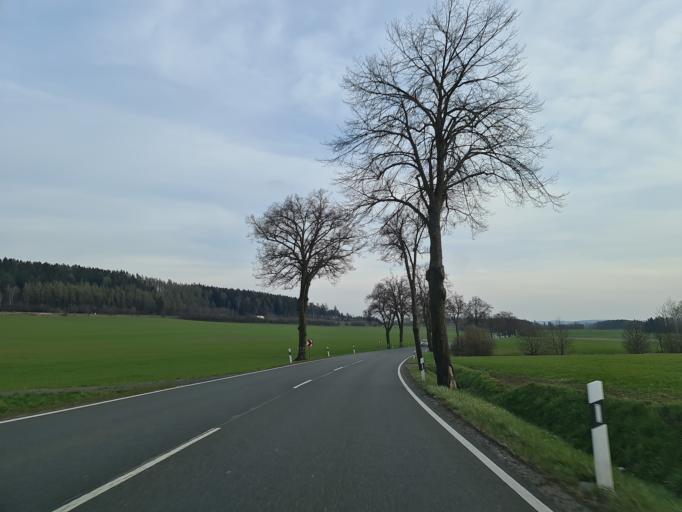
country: DE
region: Saxony
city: Oelsnitz
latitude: 50.4524
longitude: 12.1636
